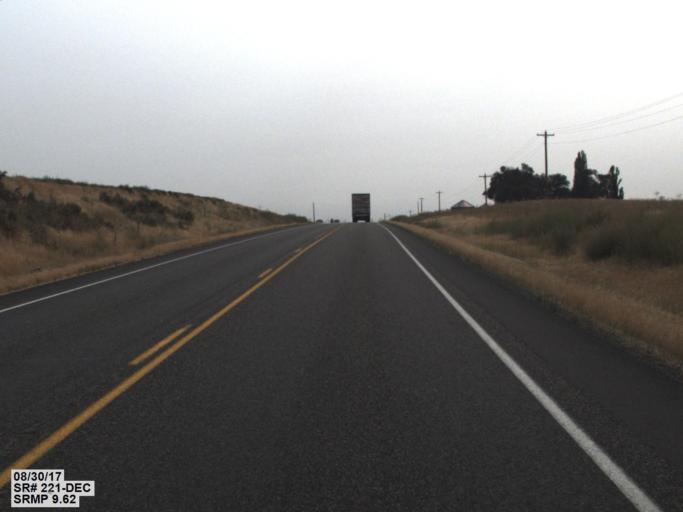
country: US
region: Oregon
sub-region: Morrow County
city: Irrigon
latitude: 46.0745
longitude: -119.6021
